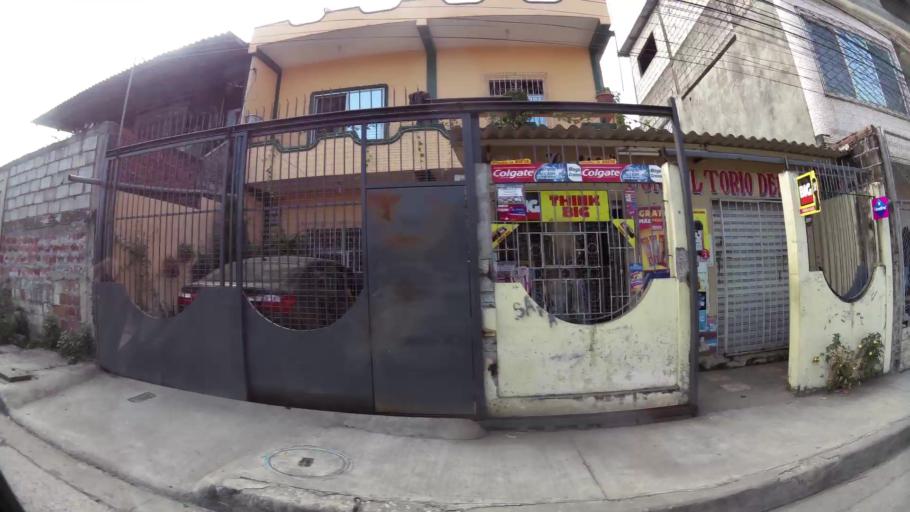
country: EC
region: Guayas
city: Santa Lucia
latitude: -2.1411
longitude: -79.9412
